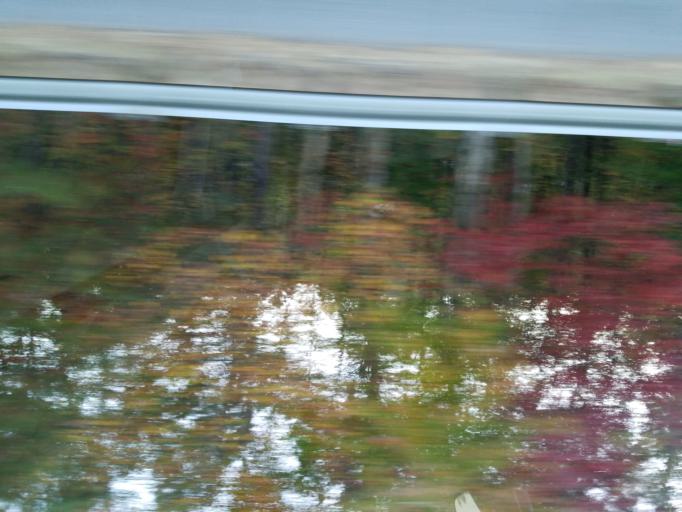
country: US
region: Georgia
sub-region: Dawson County
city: Dawsonville
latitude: 34.3400
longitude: -84.0547
